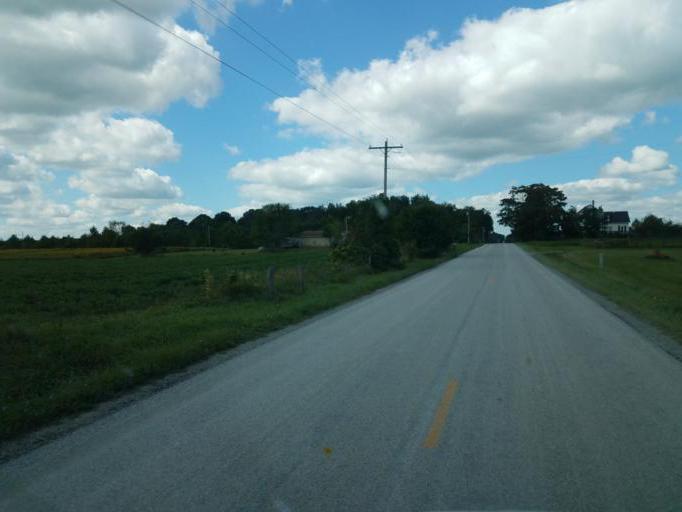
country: US
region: Ohio
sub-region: Wayne County
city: West Salem
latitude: 40.9920
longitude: -82.1509
